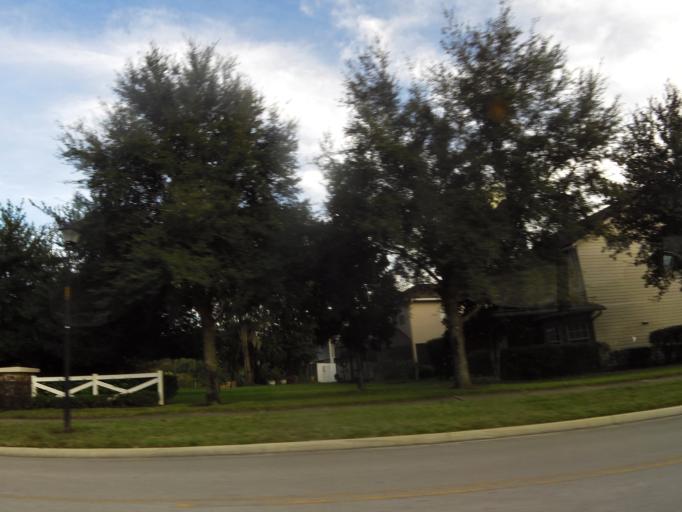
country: US
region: Florida
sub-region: Saint Johns County
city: Fruit Cove
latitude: 30.1584
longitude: -81.5486
